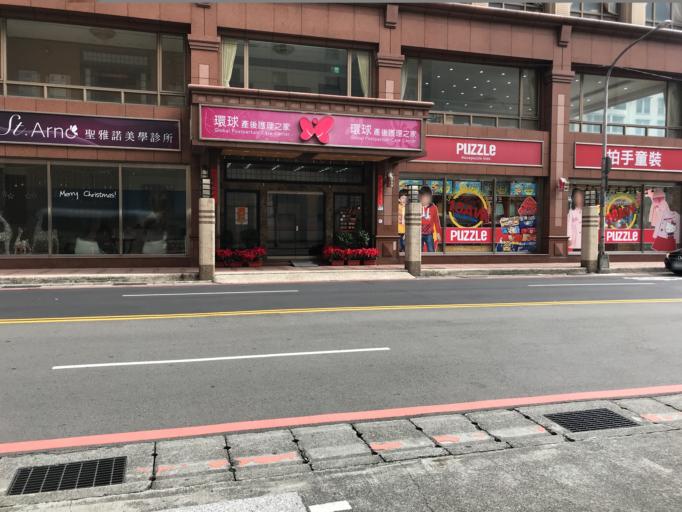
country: TW
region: Taipei
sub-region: Taipei
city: Banqiao
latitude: 25.0078
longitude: 121.4753
